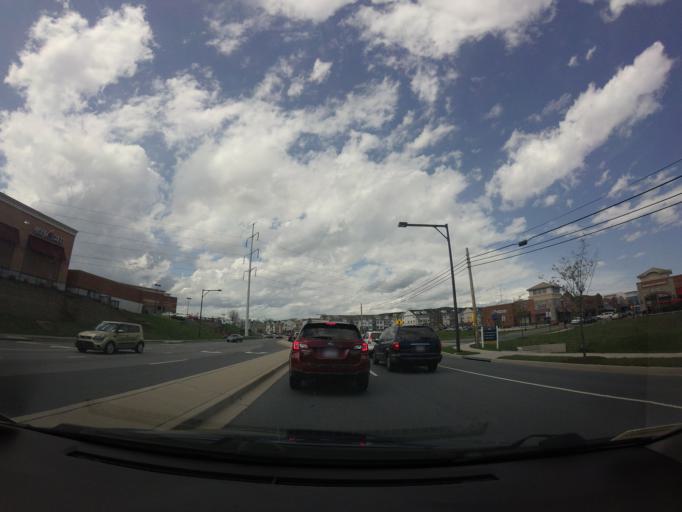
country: US
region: Maryland
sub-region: Frederick County
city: Clover Hill
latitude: 39.4464
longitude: -77.3960
